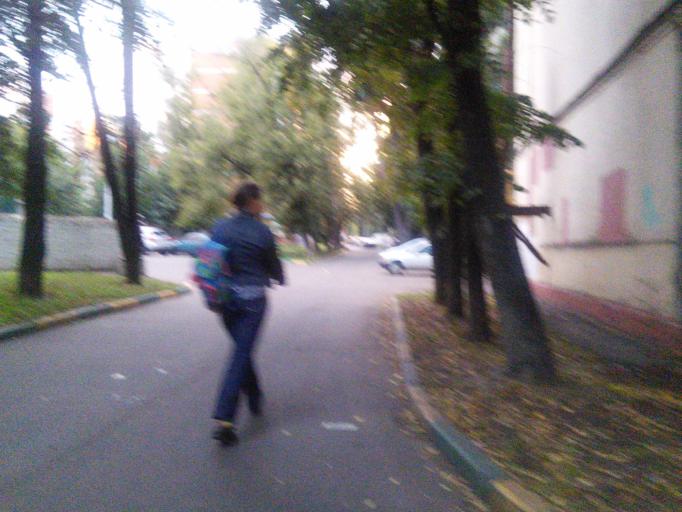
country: RU
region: Moskovskaya
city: Fili
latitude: 55.7509
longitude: 37.5056
